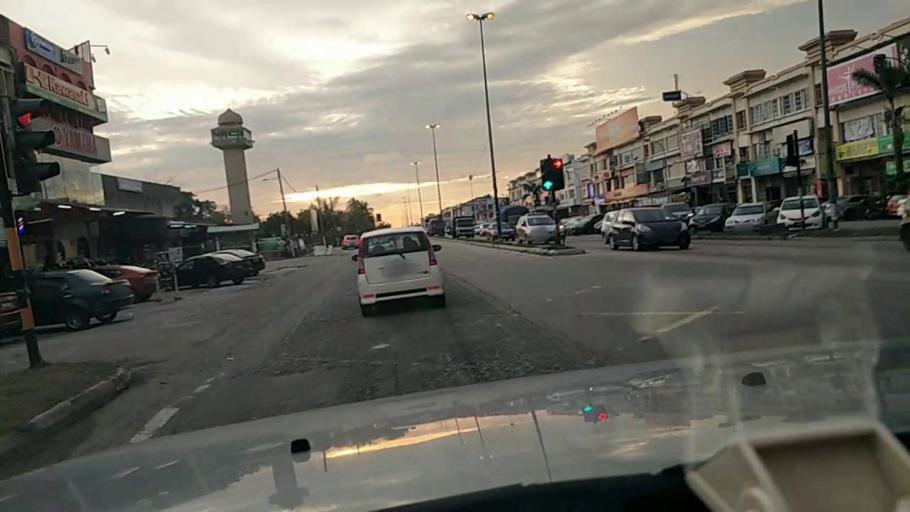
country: MY
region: Perak
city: Kampong Dungun
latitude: 3.1382
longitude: 101.3713
